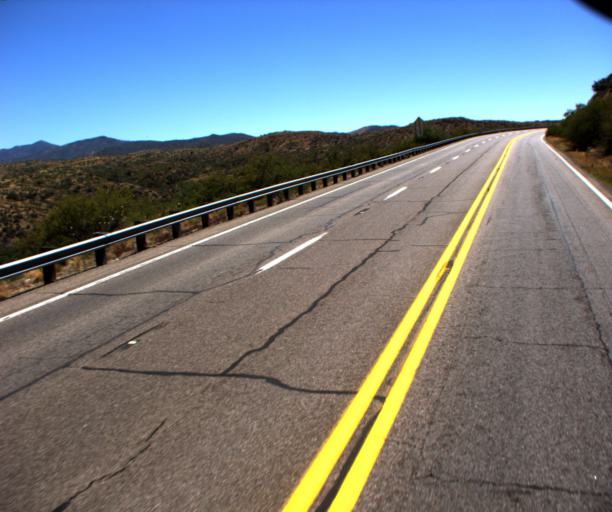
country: US
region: Arizona
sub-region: Pinal County
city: Oracle
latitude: 32.6388
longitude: -110.7254
